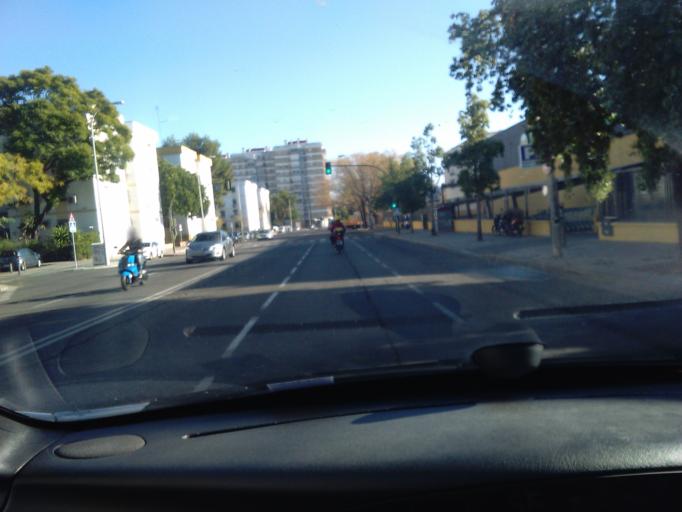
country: ES
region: Andalusia
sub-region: Provincia de Sevilla
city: Sevilla
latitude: 37.3926
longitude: -5.9613
